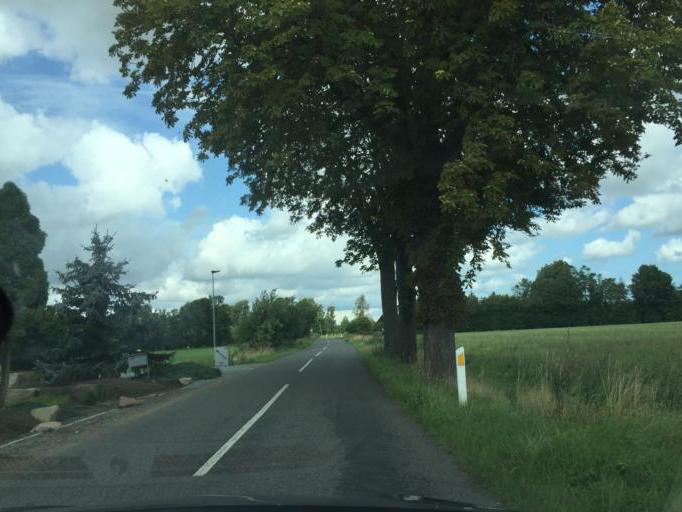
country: DK
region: South Denmark
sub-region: Odense Kommune
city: Stige
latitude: 55.4729
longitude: 10.3813
